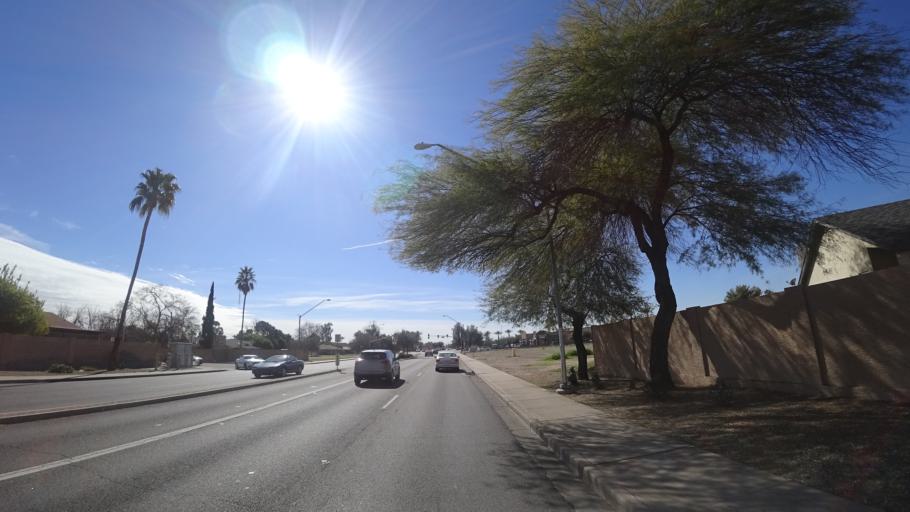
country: US
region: Arizona
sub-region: Maricopa County
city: Glendale
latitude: 33.5860
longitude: -112.1862
